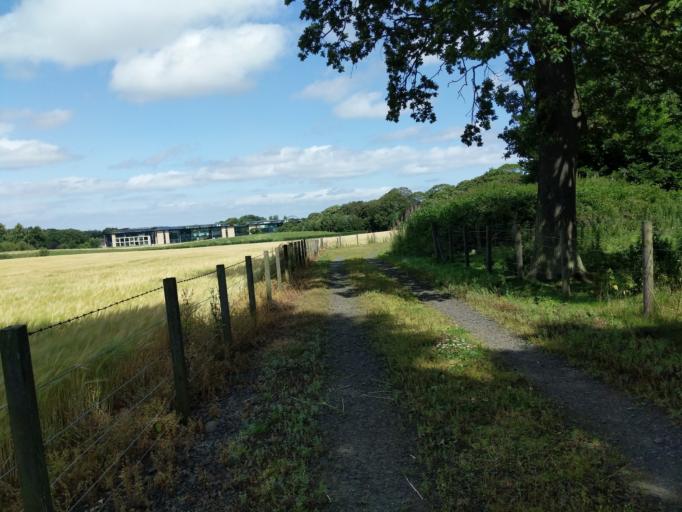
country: GB
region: Scotland
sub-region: Edinburgh
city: Currie
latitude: 55.9299
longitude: -3.3335
